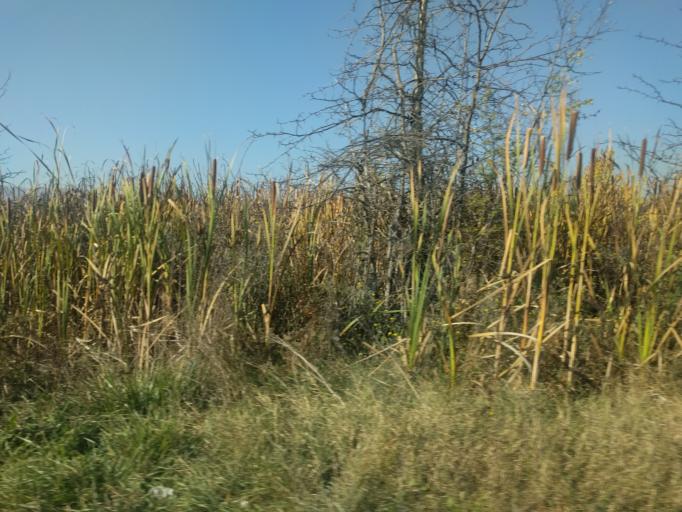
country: XK
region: Pristina
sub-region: Komuna e Gracanices
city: Glanica
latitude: 42.5899
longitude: 21.0177
